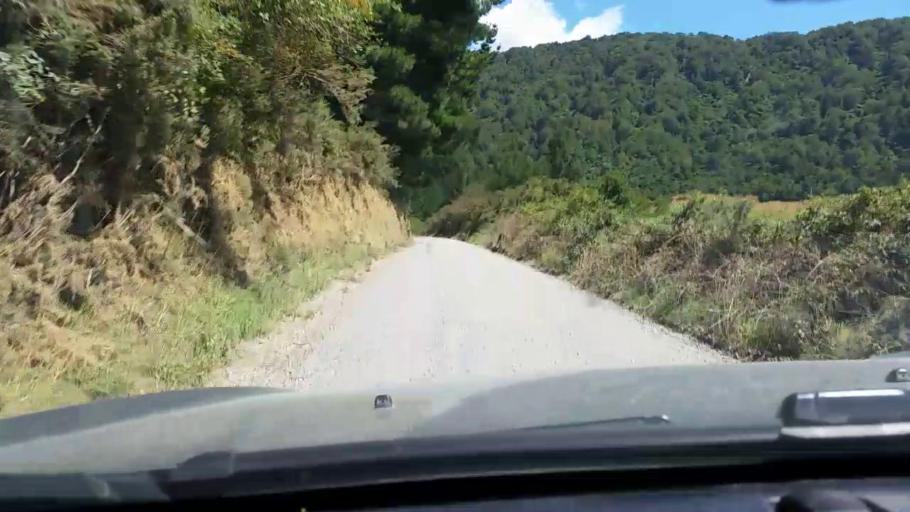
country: NZ
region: Bay of Plenty
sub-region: Rotorua District
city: Rotorua
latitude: -38.2337
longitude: 176.1619
